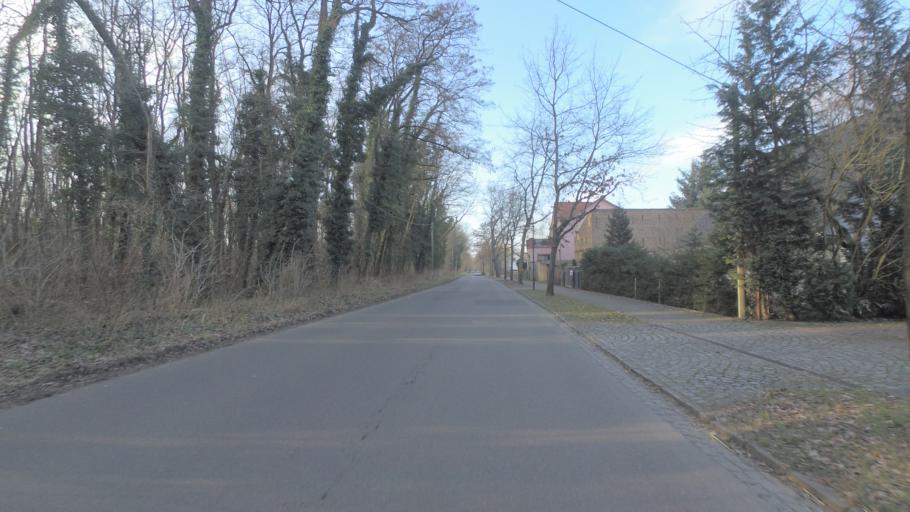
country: DE
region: Brandenburg
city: Rangsdorf
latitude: 52.2710
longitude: 13.4589
